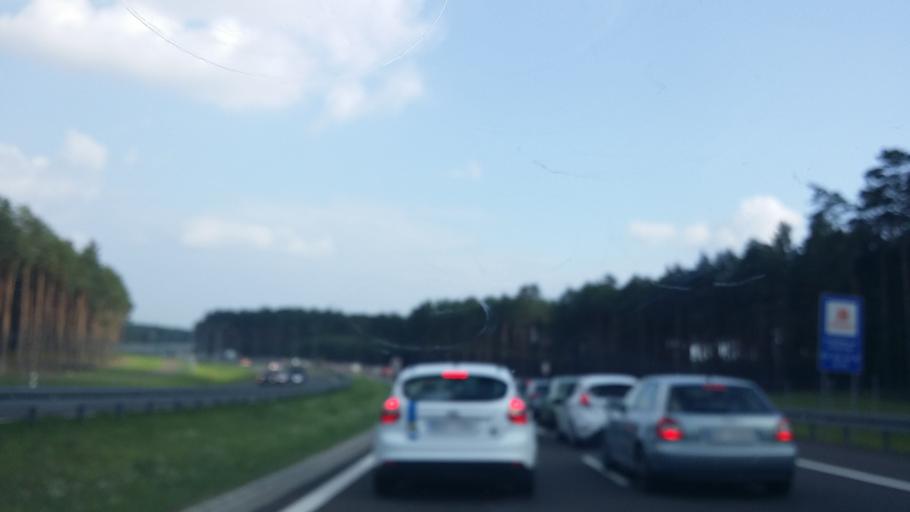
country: PL
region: Lubusz
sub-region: Powiat miedzyrzecki
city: Miedzyrzecz
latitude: 52.4743
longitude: 15.5538
